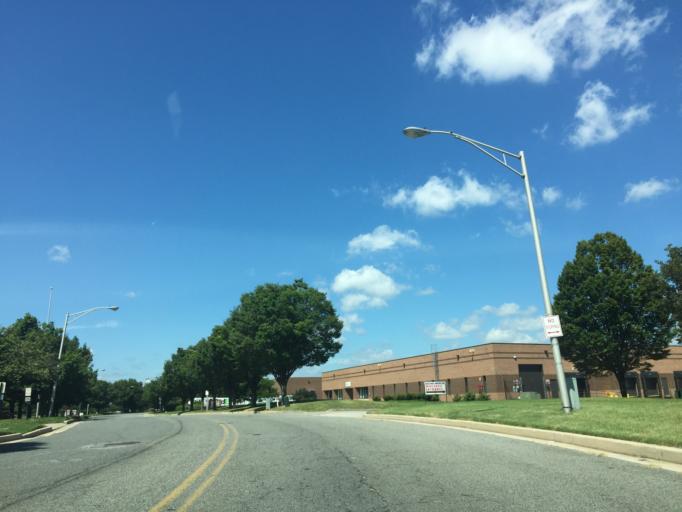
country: US
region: Maryland
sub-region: Baltimore County
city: Dundalk
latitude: 39.2709
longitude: -76.5327
